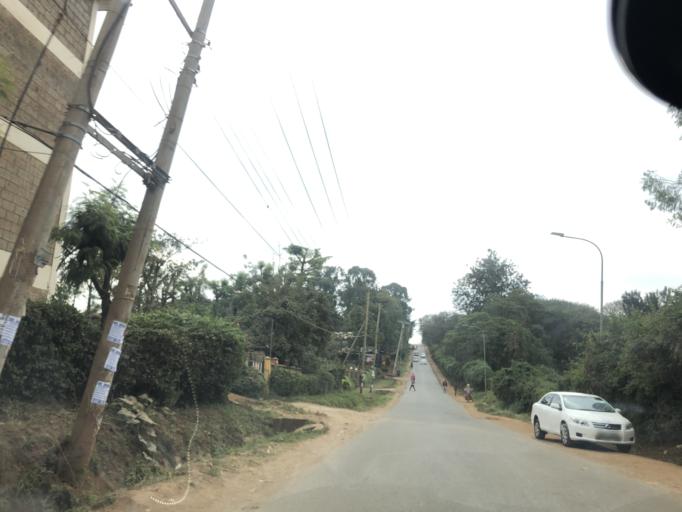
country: KE
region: Kiambu
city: Kiambu
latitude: -1.2130
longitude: 36.8926
